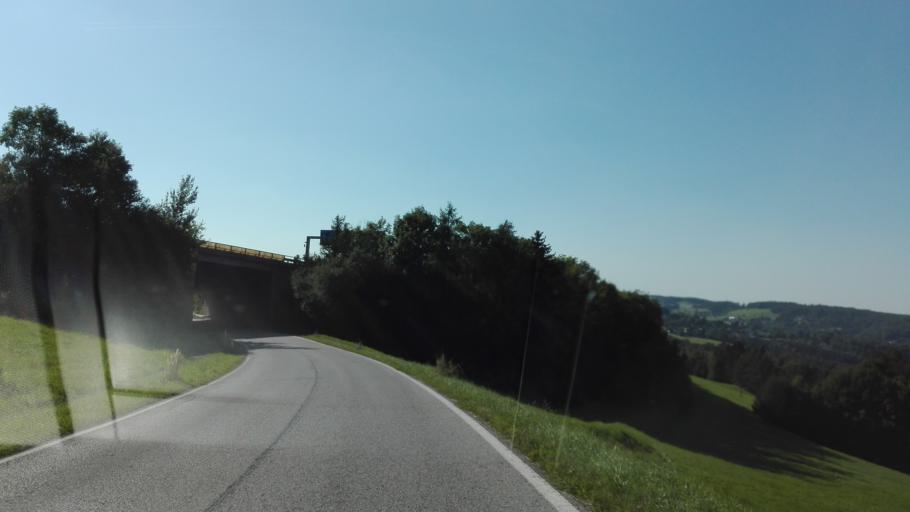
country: AT
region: Lower Austria
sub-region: Politischer Bezirk Sankt Polten
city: Eichgraben
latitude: 48.1472
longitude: 15.9836
